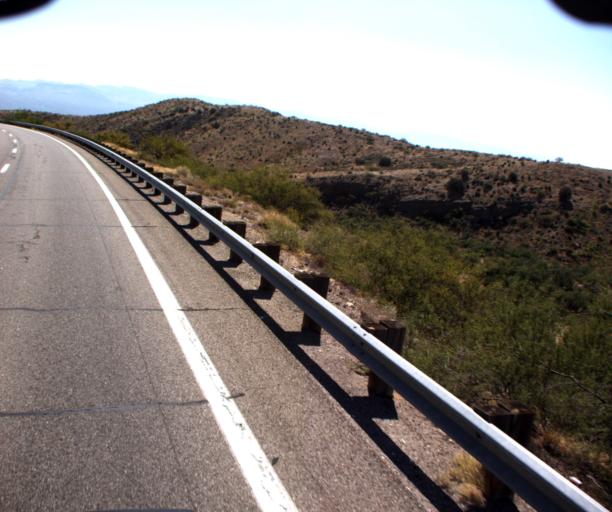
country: US
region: Arizona
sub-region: Pinal County
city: Oracle
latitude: 32.6376
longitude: -110.7275
